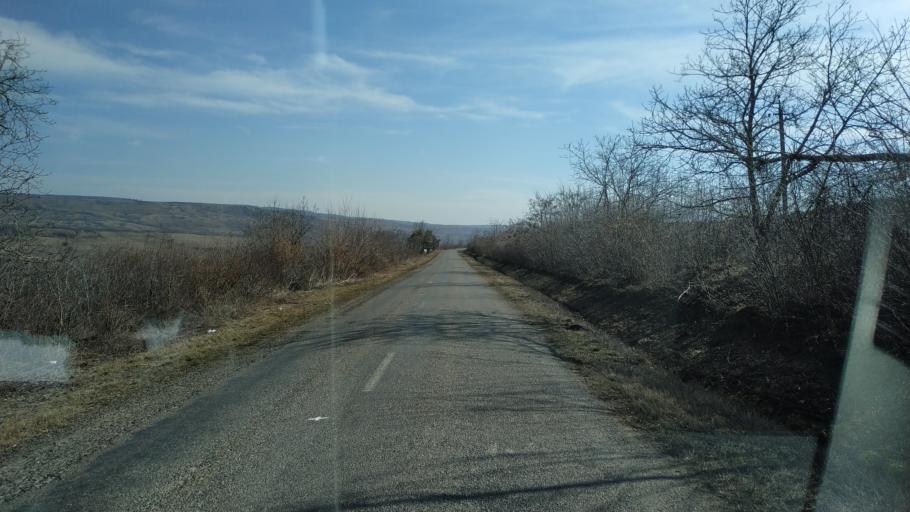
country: MD
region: Nisporeni
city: Nisporeni
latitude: 47.1788
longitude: 28.0817
